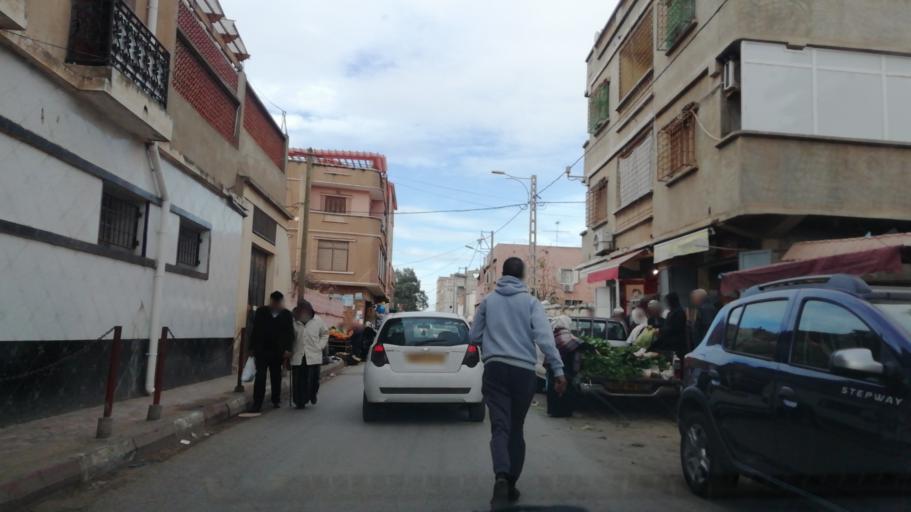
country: DZ
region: Oran
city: Oran
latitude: 35.6836
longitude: -0.6011
